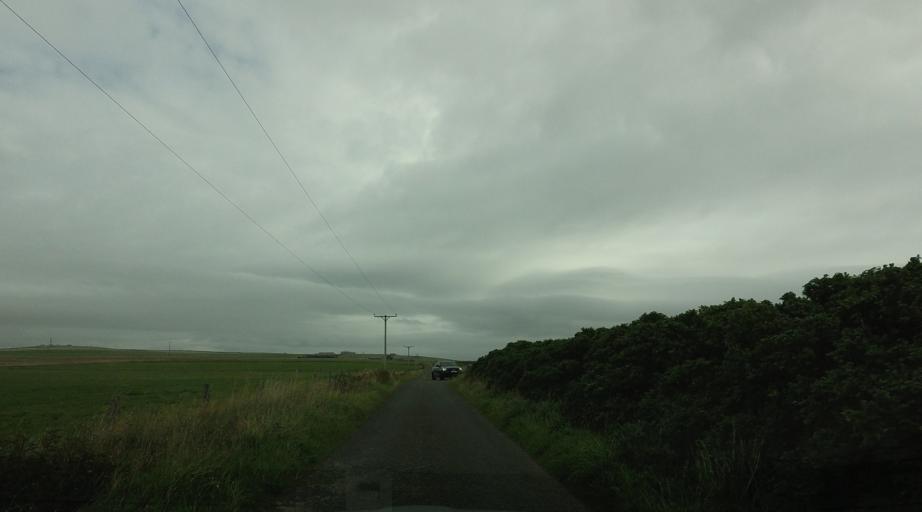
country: GB
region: Scotland
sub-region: Orkney Islands
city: Orkney
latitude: 58.7646
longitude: -2.9598
